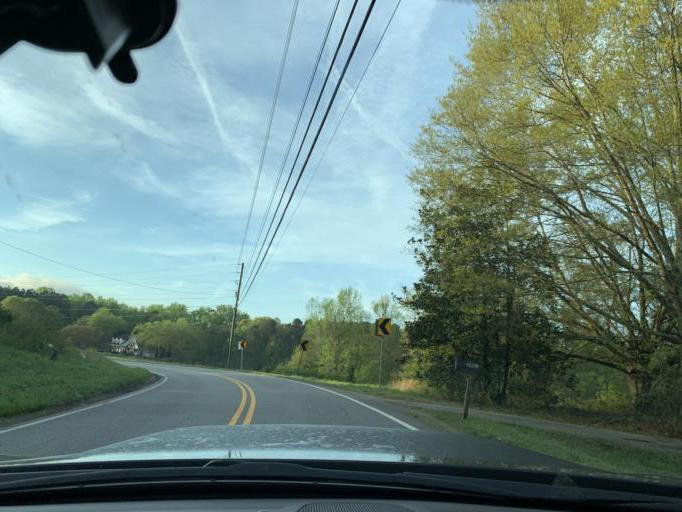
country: US
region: Georgia
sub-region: Forsyth County
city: Cumming
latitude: 34.2516
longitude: -84.1969
